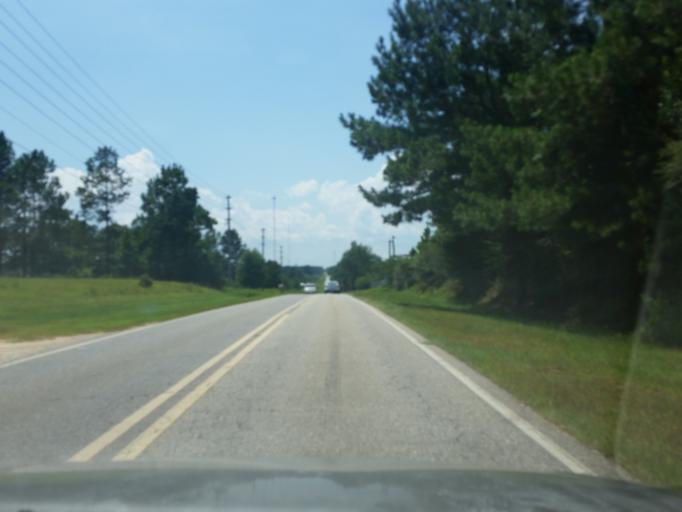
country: US
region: Alabama
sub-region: Baldwin County
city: Robertsdale
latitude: 30.6261
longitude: -87.6271
